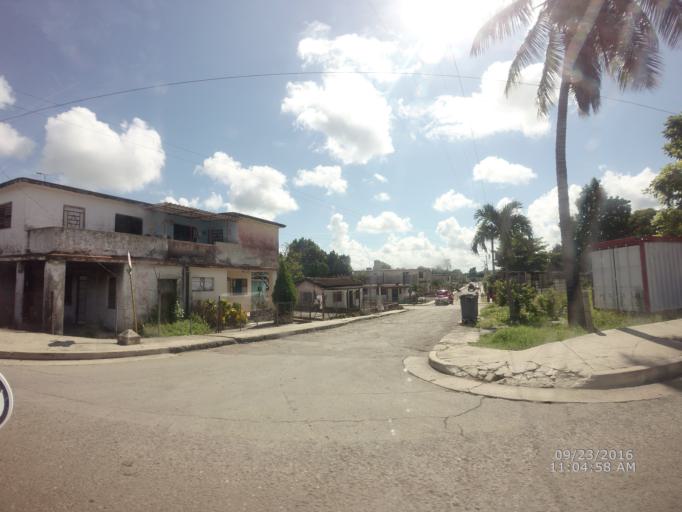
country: CU
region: Mayabeque
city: Jamaica
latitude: 23.0048
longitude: -82.2166
